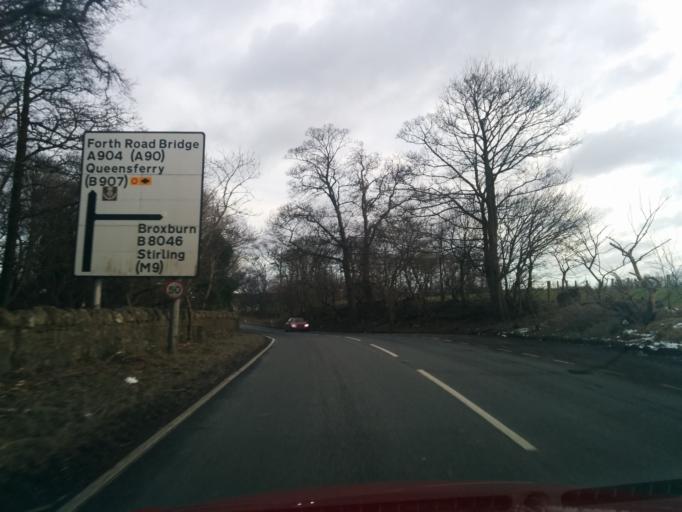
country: GB
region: Scotland
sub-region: Fife
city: Limekilns
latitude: 55.9841
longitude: -3.5139
